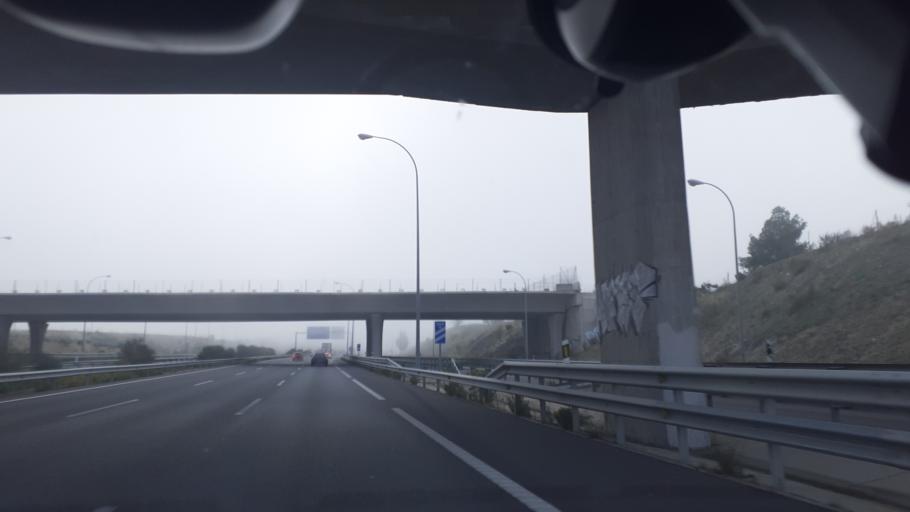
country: ES
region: Madrid
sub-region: Provincia de Madrid
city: Vicalvaro
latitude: 40.3837
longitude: -3.5879
